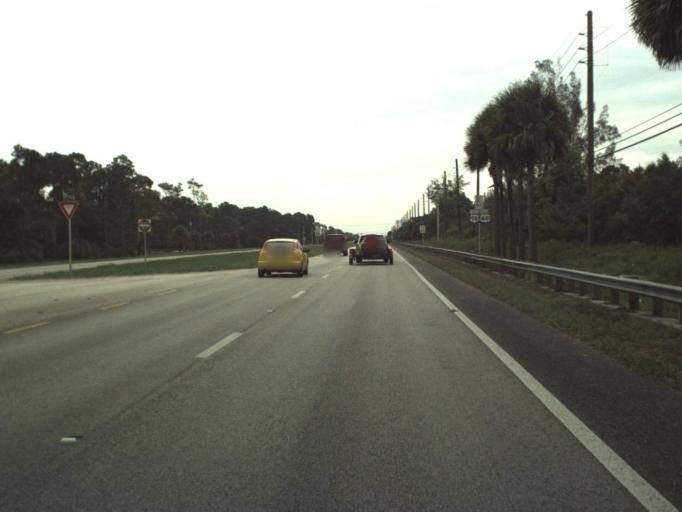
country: US
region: Florida
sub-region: Palm Beach County
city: Loxahatchee Groves
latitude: 26.6822
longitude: -80.2670
